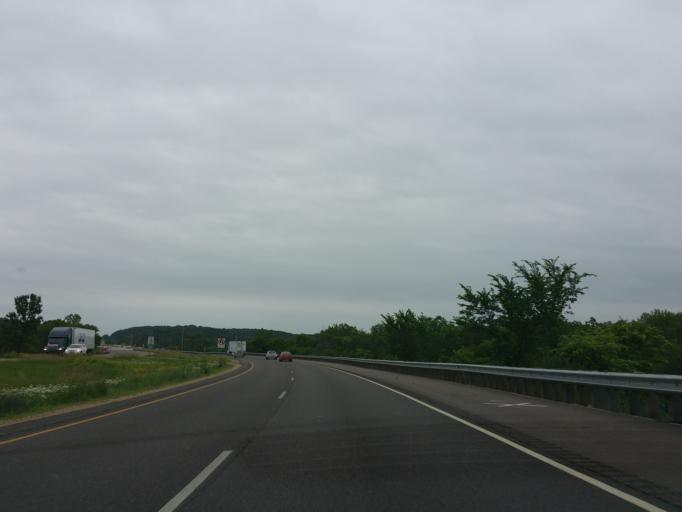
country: US
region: Wisconsin
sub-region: Eau Claire County
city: Eau Claire
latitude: 44.7828
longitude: -91.5423
